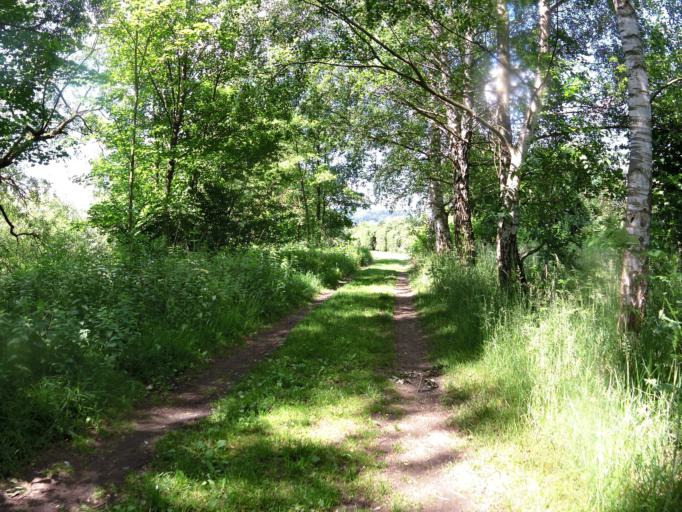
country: DE
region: Hesse
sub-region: Regierungsbezirk Kassel
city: Bad Hersfeld
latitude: 50.8629
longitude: 9.7111
